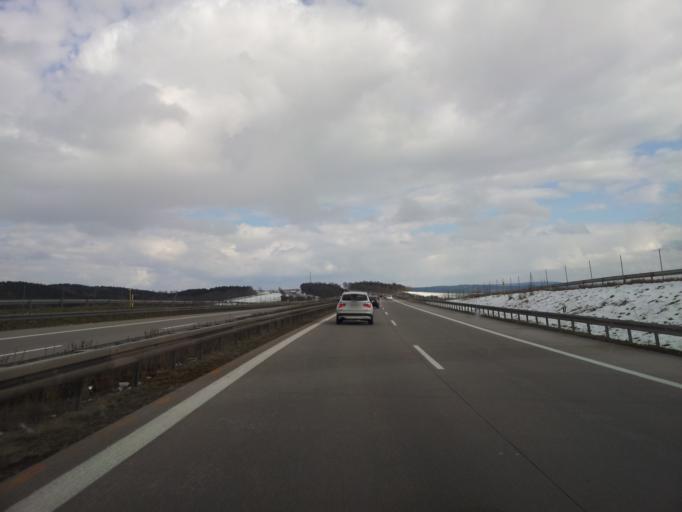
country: DE
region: Saxony
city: Wildenfels
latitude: 50.6879
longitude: 12.6120
